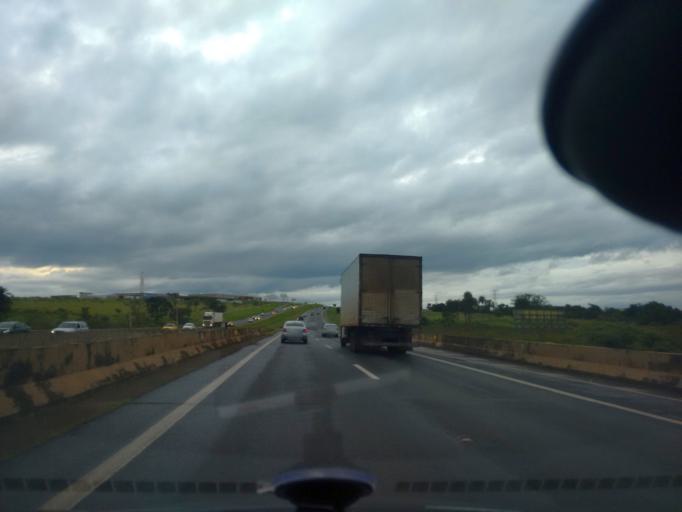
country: BR
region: Sao Paulo
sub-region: Santa Gertrudes
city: Santa Gertrudes
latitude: -22.4502
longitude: -47.5579
